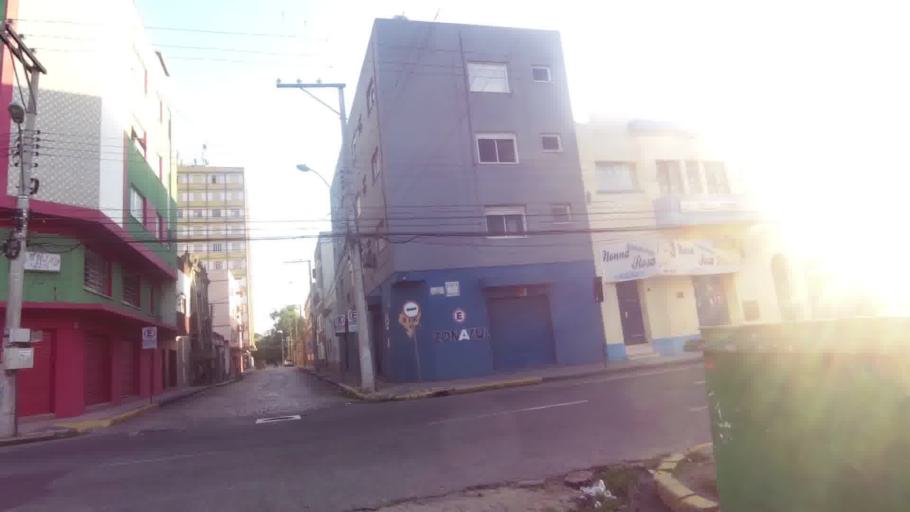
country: BR
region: Rio Grande do Sul
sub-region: Rio Grande
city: Rio Grande
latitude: -32.0313
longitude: -52.0912
